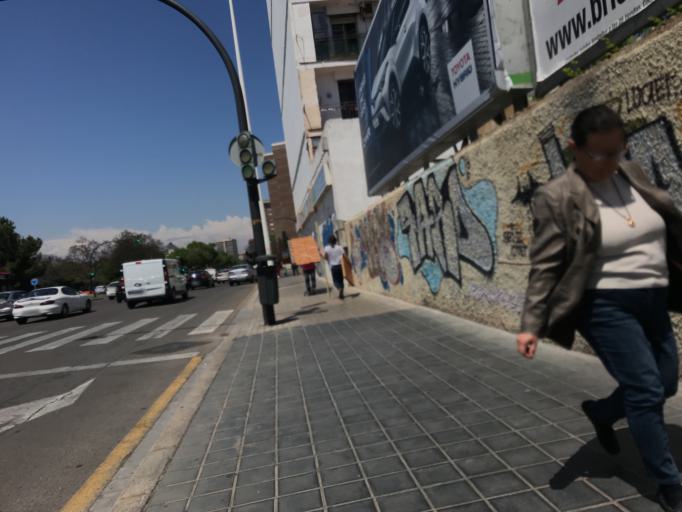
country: ES
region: Valencia
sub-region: Provincia de Valencia
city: Mislata
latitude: 39.4628
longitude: -0.4051
